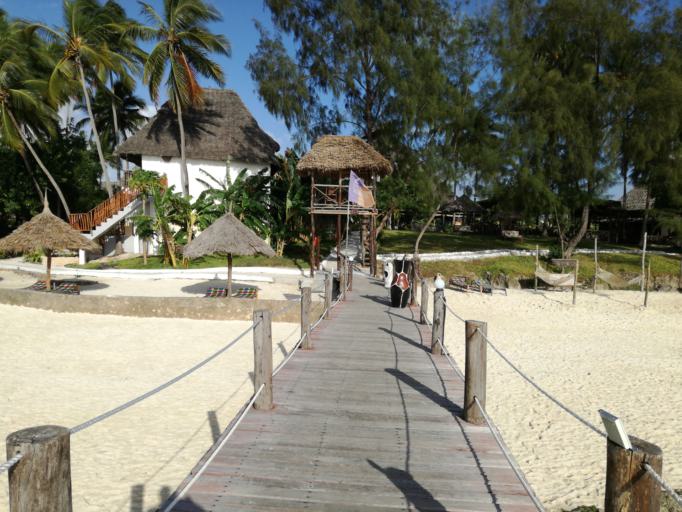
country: TZ
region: Zanzibar Central/South
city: Koani
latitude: -6.1354
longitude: 39.4258
